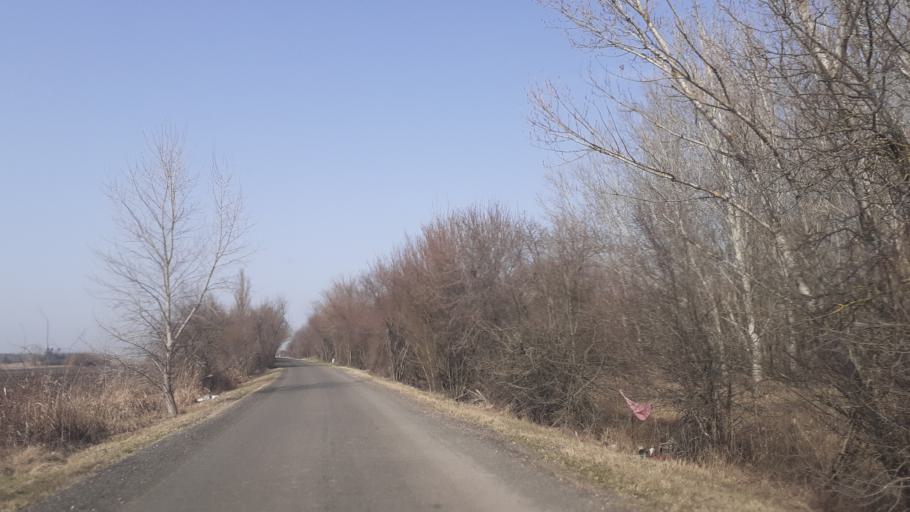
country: HU
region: Pest
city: Dabas
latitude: 47.1098
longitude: 19.2224
